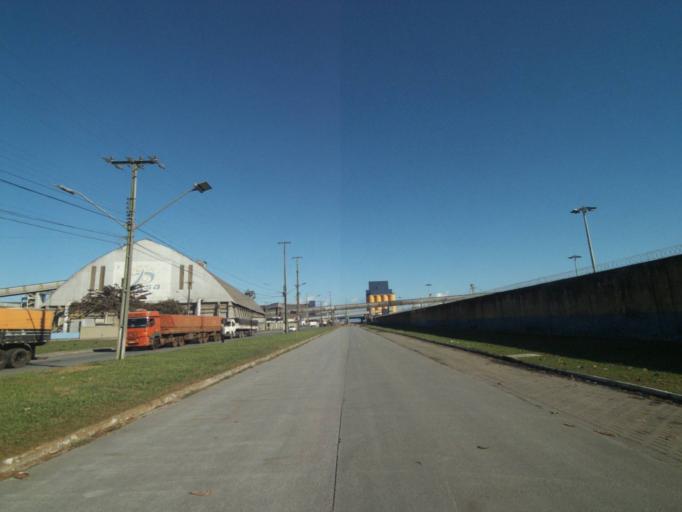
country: BR
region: Parana
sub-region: Paranagua
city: Paranagua
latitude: -25.5036
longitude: -48.5204
